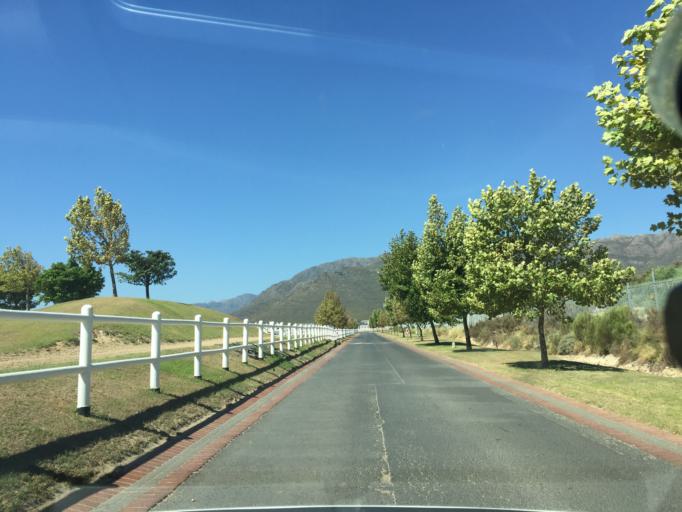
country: ZA
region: Western Cape
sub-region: Cape Winelands District Municipality
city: Paarl
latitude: -33.8061
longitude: 18.9701
